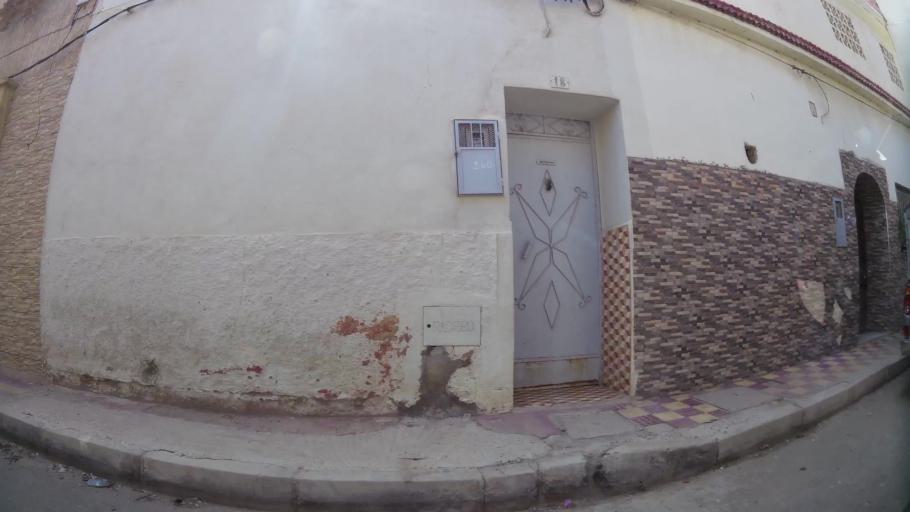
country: MA
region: Oriental
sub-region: Oujda-Angad
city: Oujda
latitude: 34.6840
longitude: -1.9063
